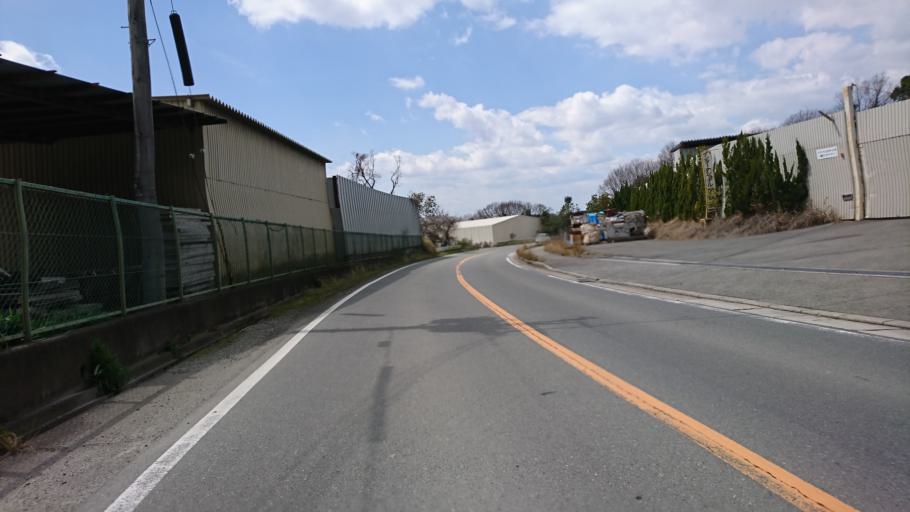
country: JP
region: Hyogo
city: Miki
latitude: 34.7672
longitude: 134.9577
